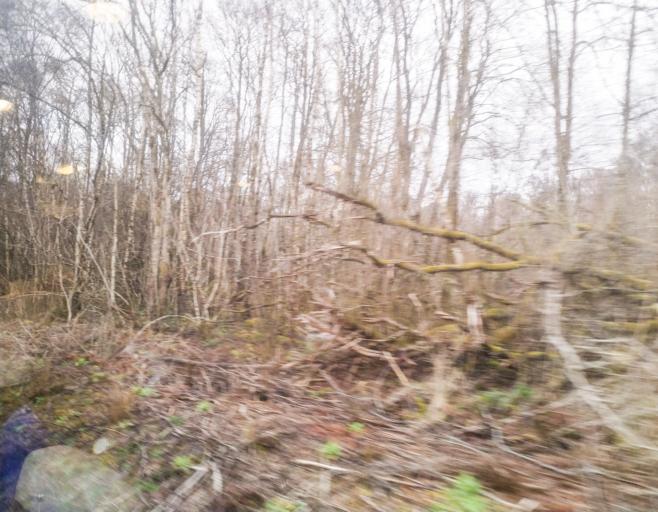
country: GB
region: Scotland
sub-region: Highland
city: Spean Bridge
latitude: 56.8919
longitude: -4.8804
